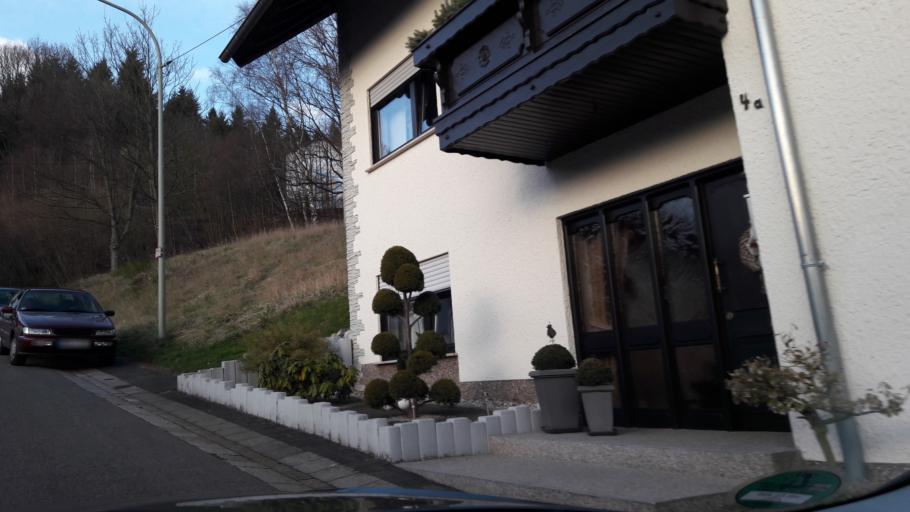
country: DE
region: Saarland
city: Oberthal
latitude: 49.5212
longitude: 7.1046
